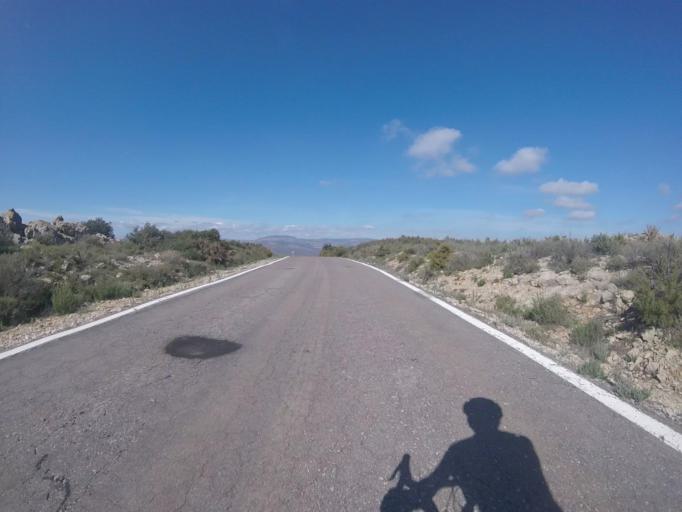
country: ES
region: Valencia
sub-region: Provincia de Castello
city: Albocasser
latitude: 40.3454
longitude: 0.0488
